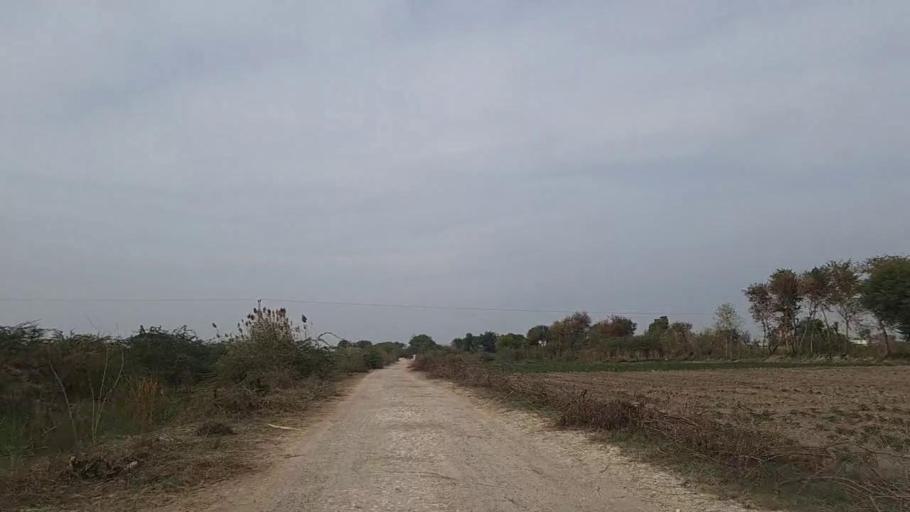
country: PK
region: Sindh
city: Daur
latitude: 26.4226
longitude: 68.4185
